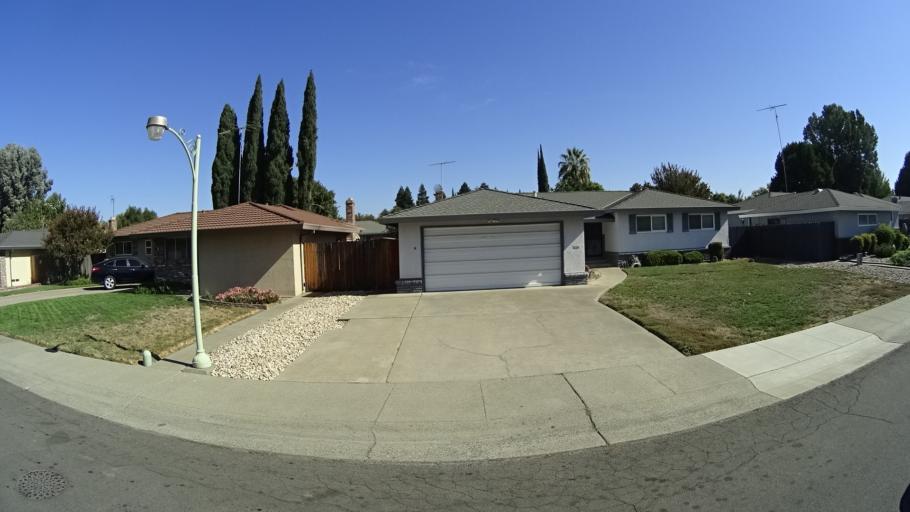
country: US
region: California
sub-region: Sacramento County
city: Parkway
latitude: 38.4981
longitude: -121.5211
